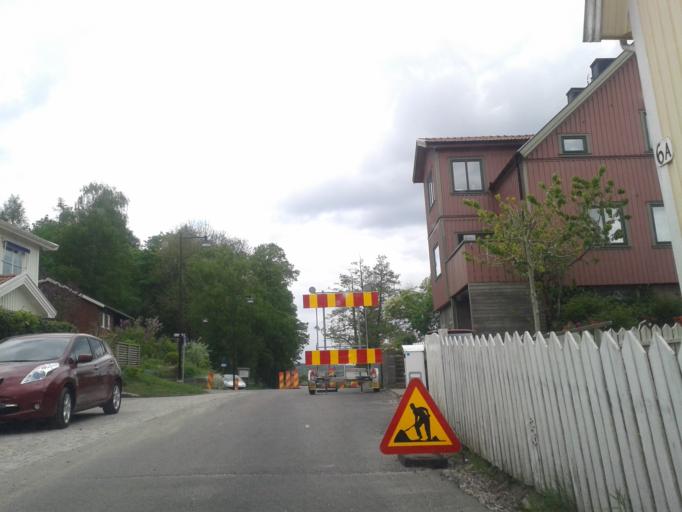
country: SE
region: Vaestra Goetaland
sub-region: Kungalvs Kommun
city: Kungalv
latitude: 57.8654
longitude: 12.0040
